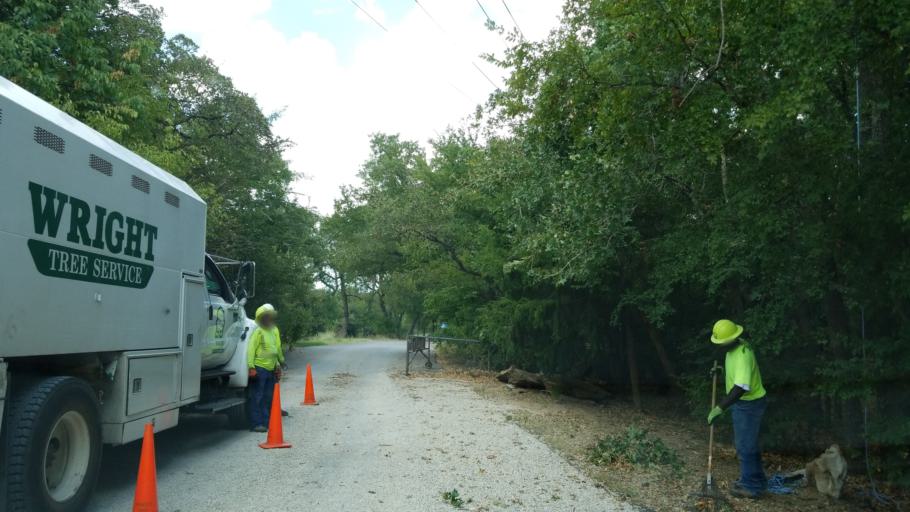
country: US
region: Texas
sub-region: Tarrant County
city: Euless
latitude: 32.8570
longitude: -97.0623
